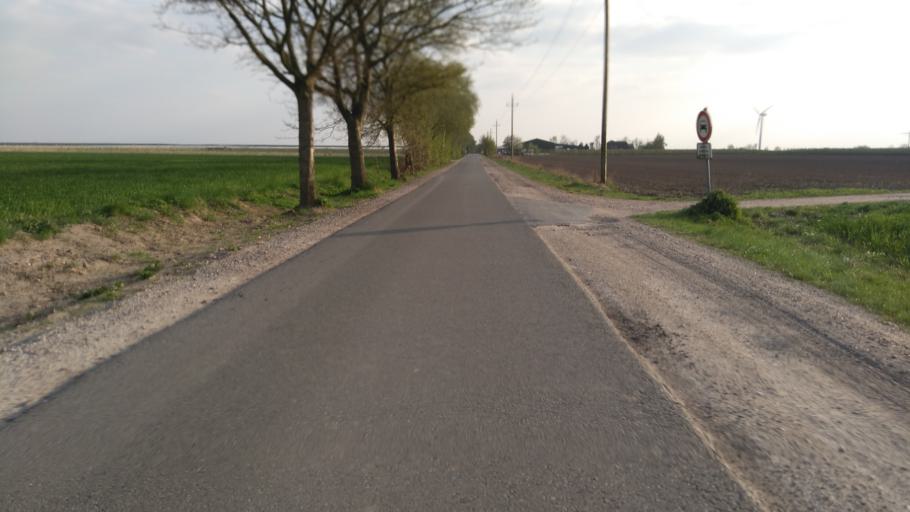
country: DE
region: Lower Saxony
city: Apensen
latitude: 53.4624
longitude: 9.6286
